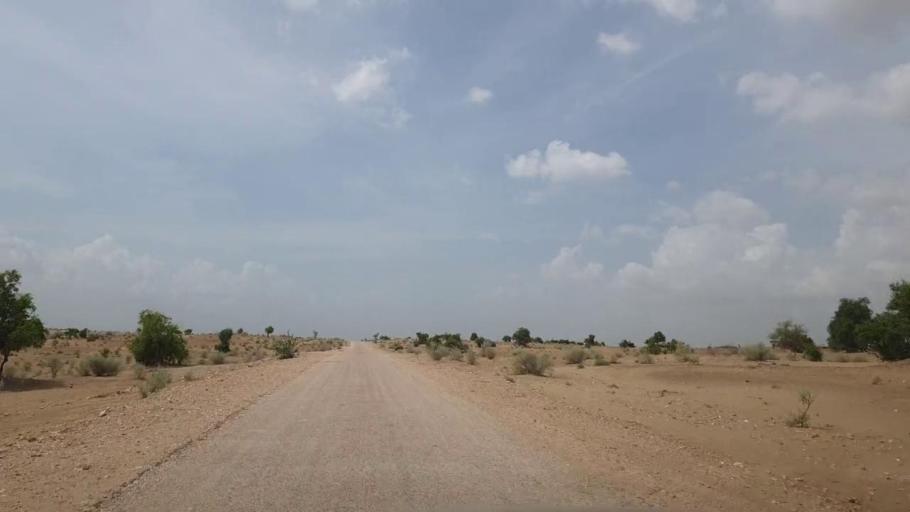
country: PK
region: Sindh
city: Kot Diji
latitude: 27.2055
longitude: 69.0854
